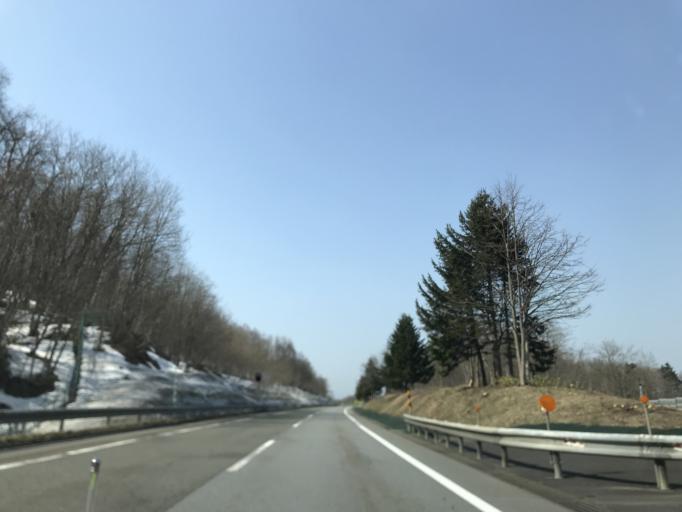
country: JP
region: Hokkaido
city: Bibai
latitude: 43.2990
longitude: 141.8750
